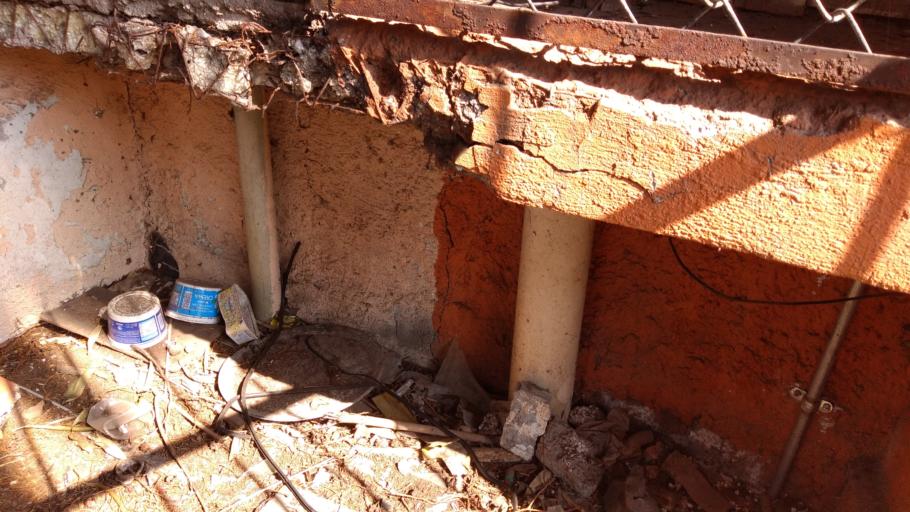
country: MX
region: Mexico City
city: Tlahuac
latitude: 19.2857
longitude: -99.0535
